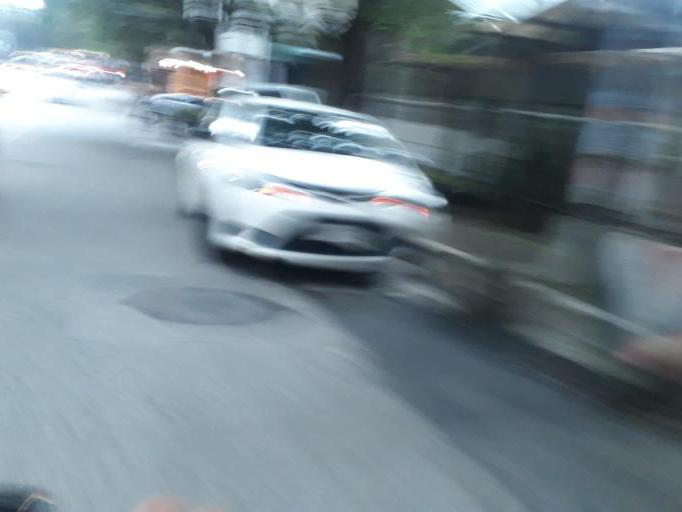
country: PH
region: Metro Manila
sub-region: Quezon City
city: Quezon City
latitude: 14.6807
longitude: 121.0802
